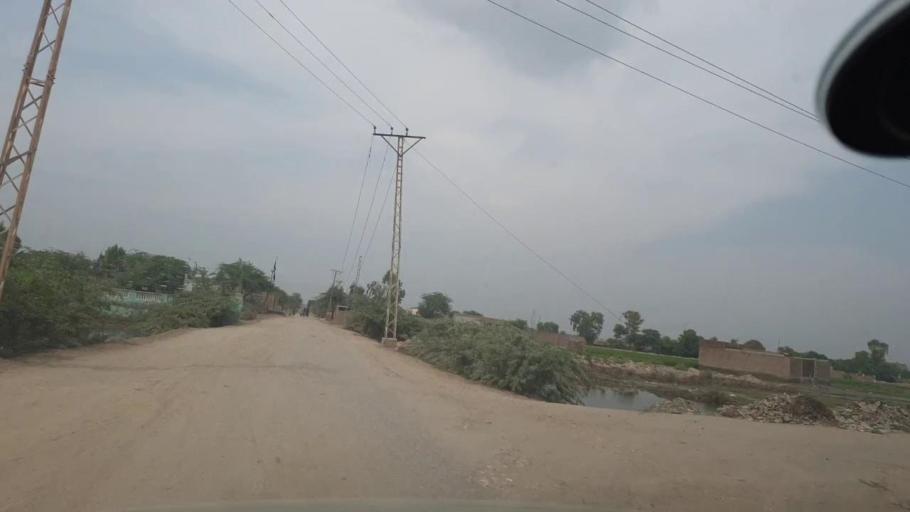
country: PK
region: Sindh
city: Jacobabad
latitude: 28.2625
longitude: 68.4375
